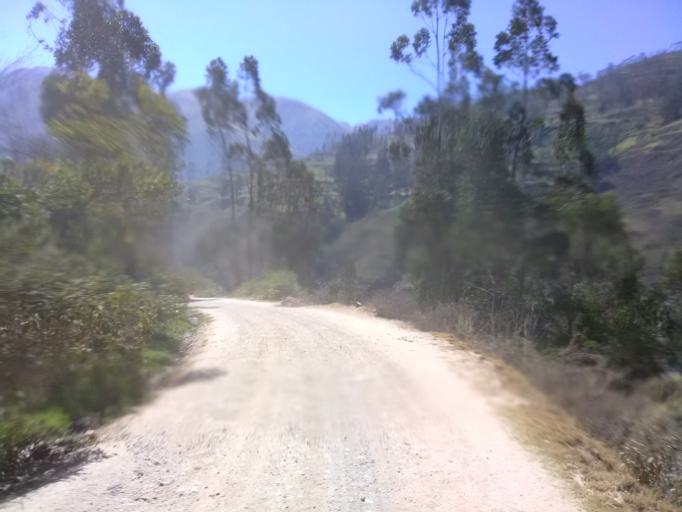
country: BO
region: Cochabamba
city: Colchani
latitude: -17.2299
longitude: -66.5340
